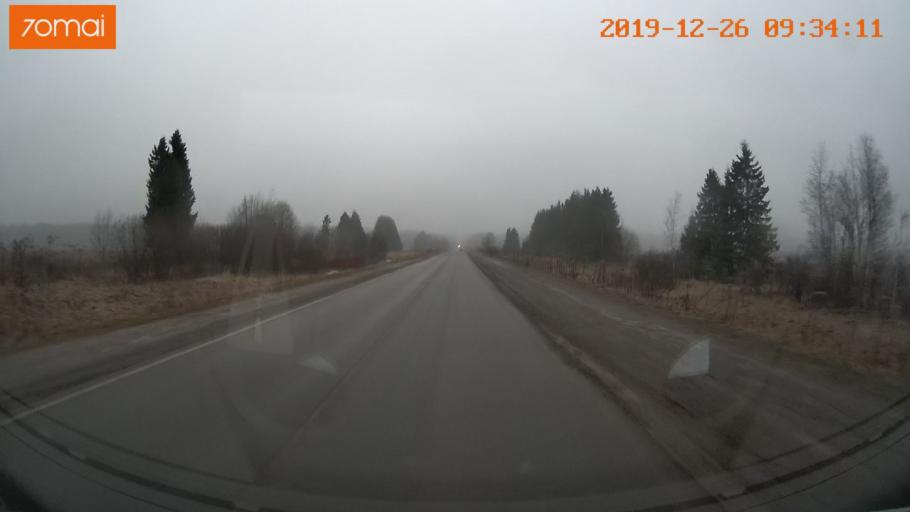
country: RU
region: Vologda
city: Vologda
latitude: 59.0985
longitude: 40.0896
